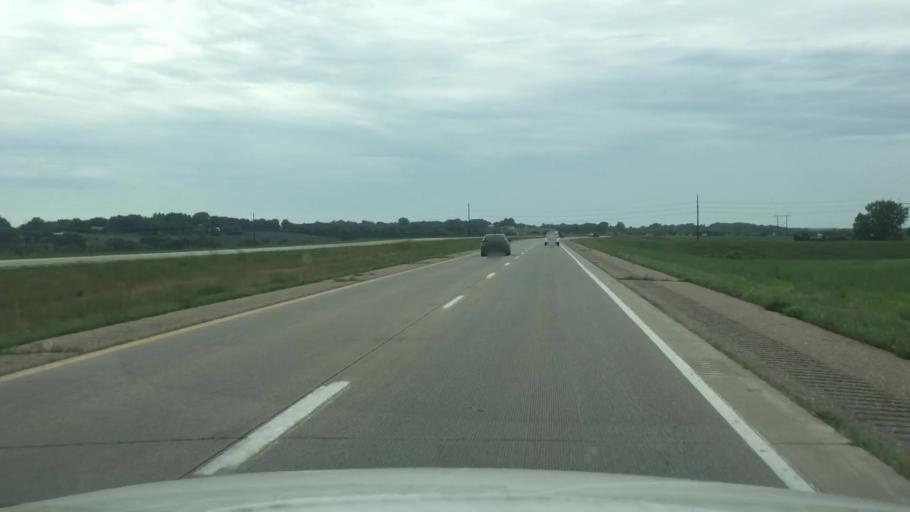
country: US
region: Iowa
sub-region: Warren County
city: Norwalk
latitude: 41.4985
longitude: -93.6202
